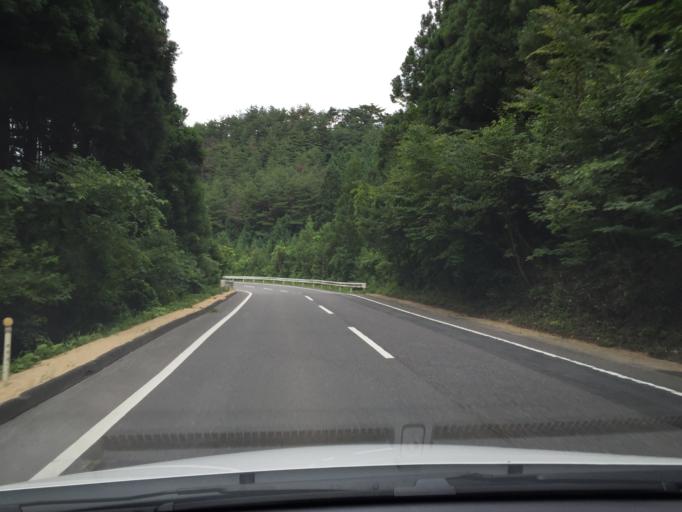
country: JP
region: Fukushima
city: Sukagawa
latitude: 37.1801
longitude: 140.1796
